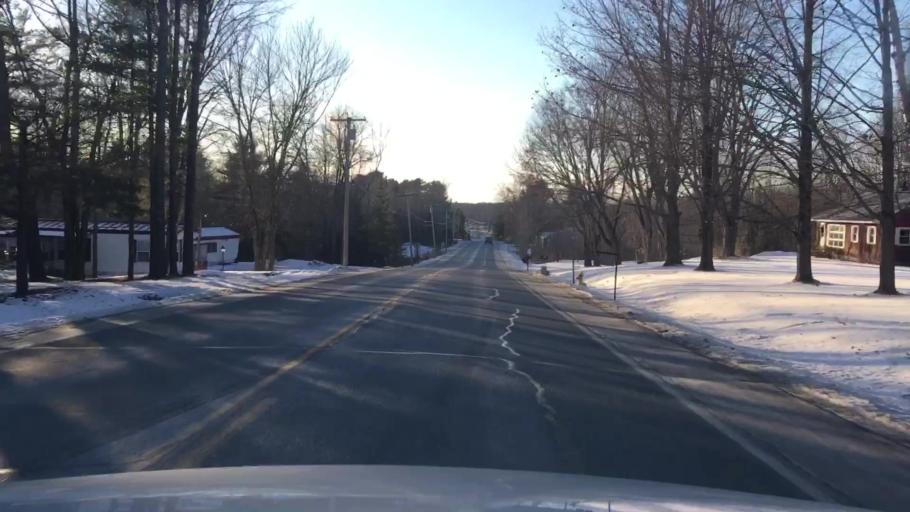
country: US
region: Maine
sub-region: Penobscot County
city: Eddington
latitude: 44.8279
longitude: -68.6837
